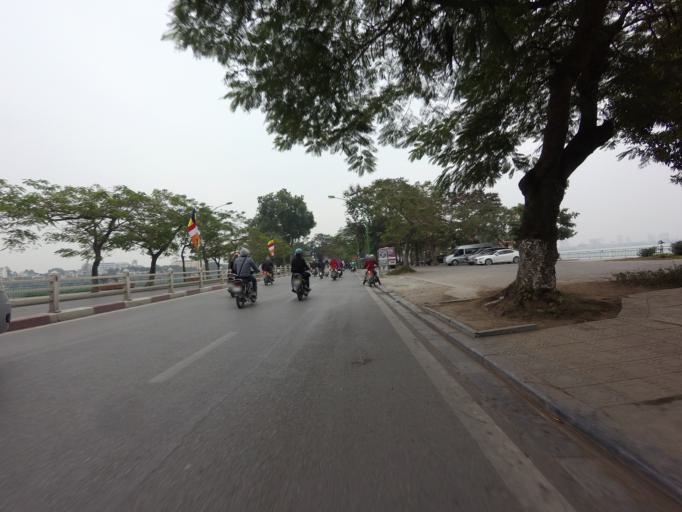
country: VN
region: Ha Noi
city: Hoan Kiem
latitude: 21.0489
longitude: 105.8386
